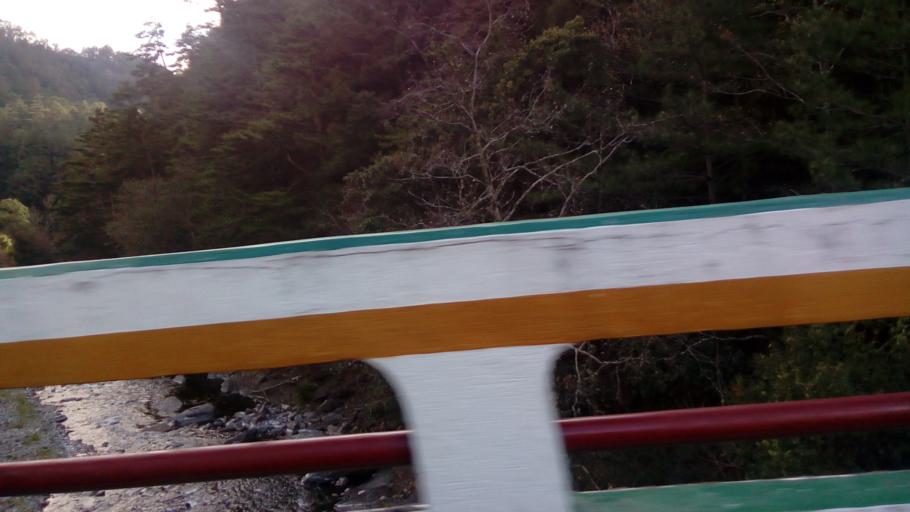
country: TW
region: Taiwan
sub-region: Hualien
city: Hualian
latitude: 24.3477
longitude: 121.3082
